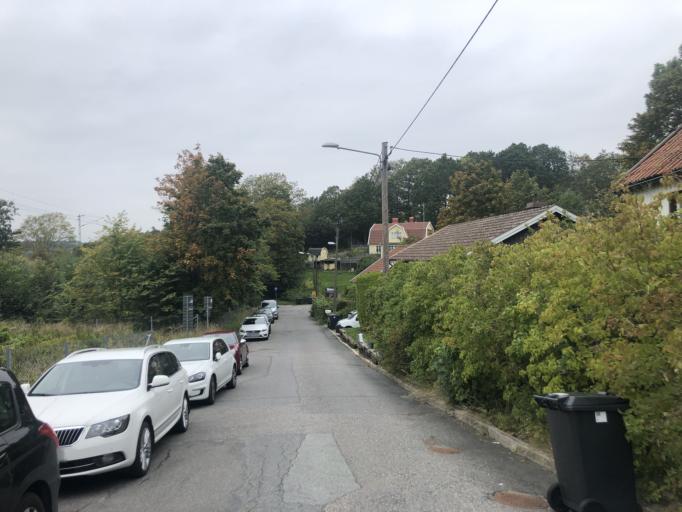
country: SE
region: Vaestra Goetaland
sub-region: Molndal
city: Moelndal
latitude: 57.6599
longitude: 12.0236
